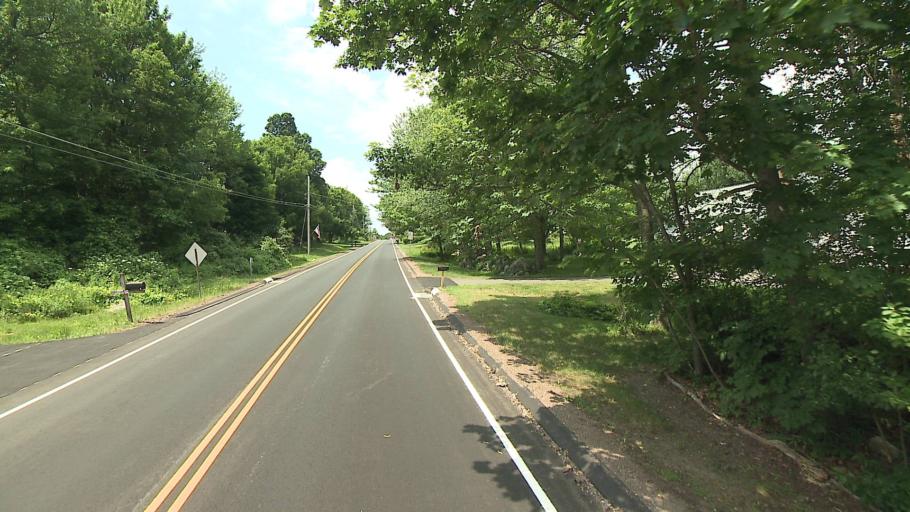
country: US
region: Connecticut
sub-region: Hartford County
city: North Granby
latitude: 41.9991
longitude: -72.9013
